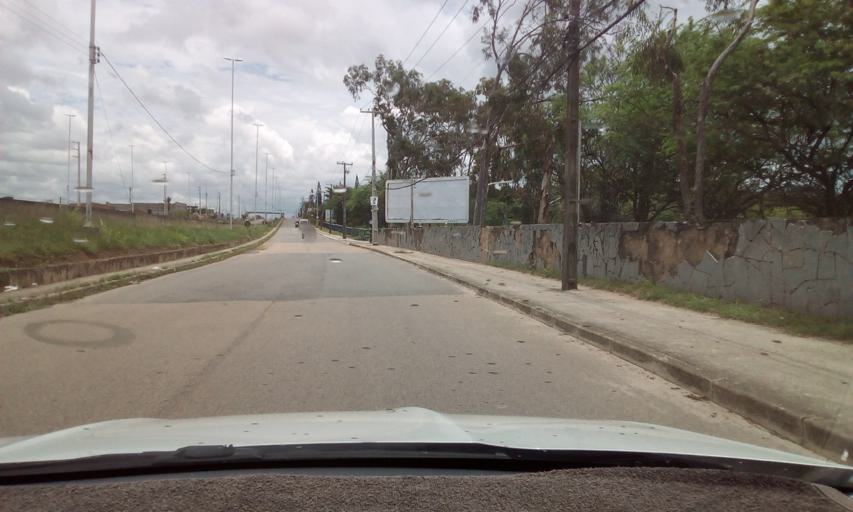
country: BR
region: Pernambuco
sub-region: Gravata
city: Gravata
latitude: -8.1926
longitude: -35.5469
